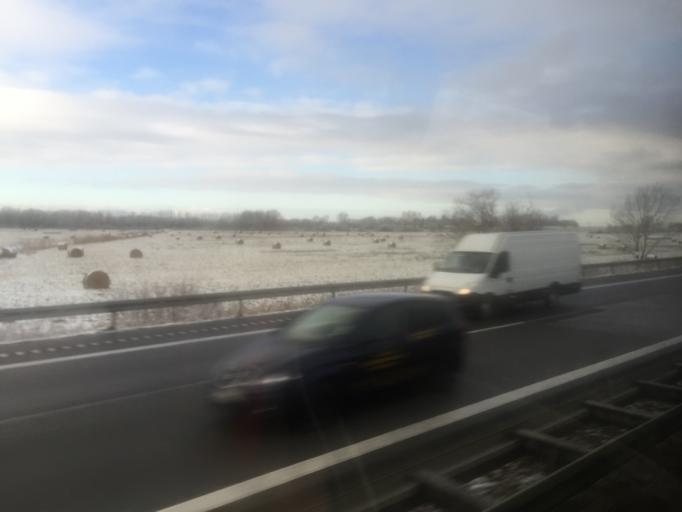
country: DE
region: Brandenburg
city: Fehrbellin
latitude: 52.8318
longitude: 12.7925
